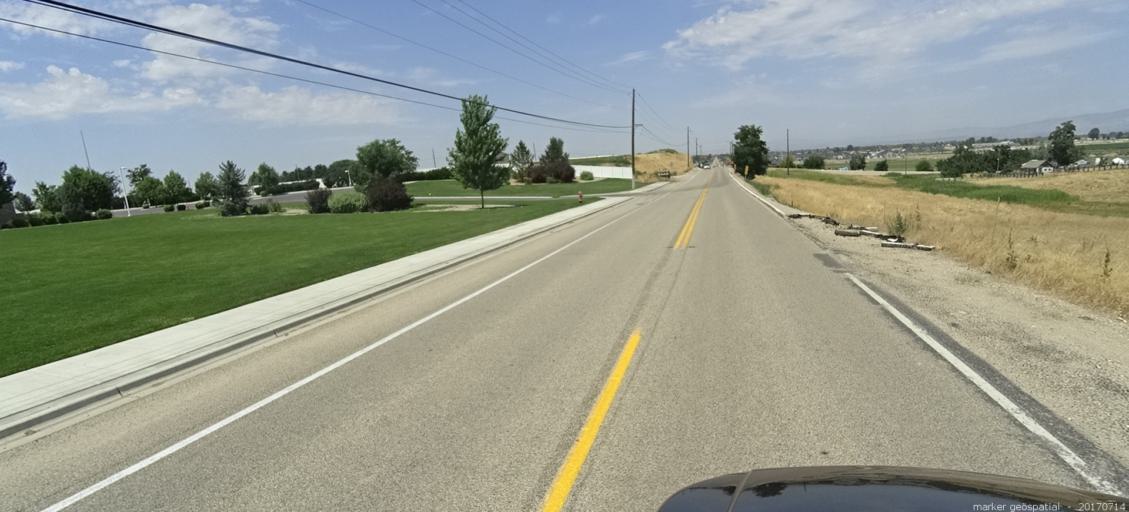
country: US
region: Idaho
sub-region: Ada County
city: Meridian
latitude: 43.5441
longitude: -116.3543
